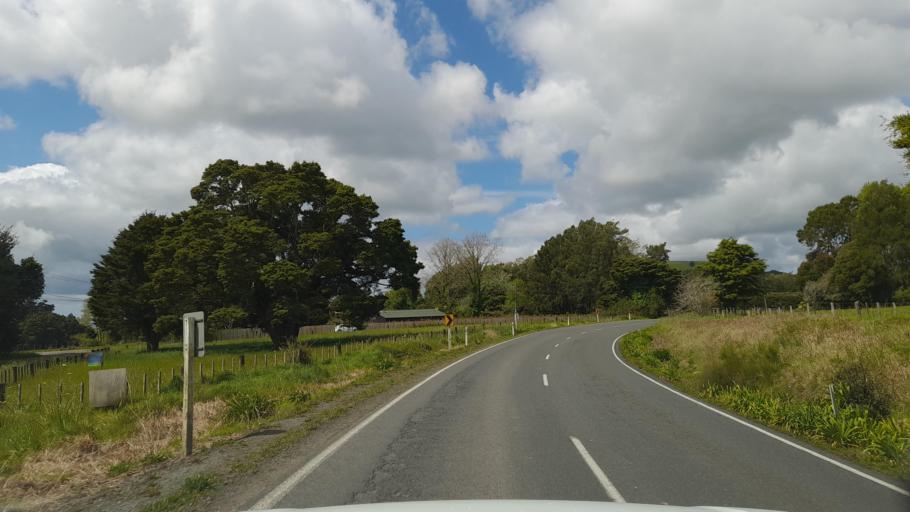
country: NZ
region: Northland
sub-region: Whangarei
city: Maungatapere
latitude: -35.6564
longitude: 174.1726
